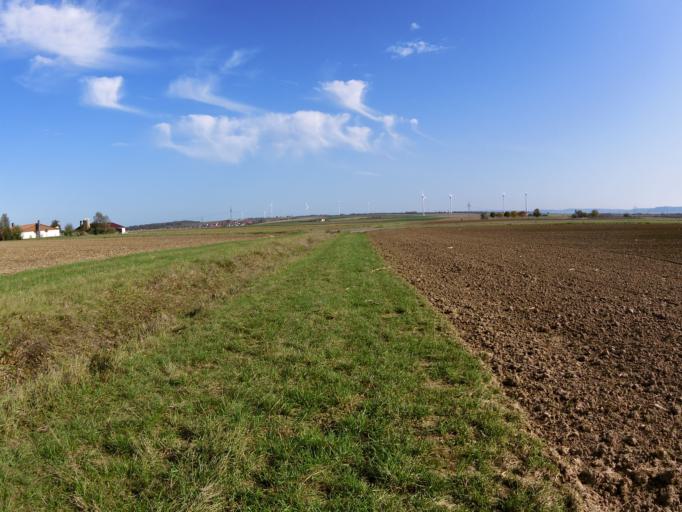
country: DE
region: Bavaria
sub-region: Regierungsbezirk Unterfranken
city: Biebelried
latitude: 49.7484
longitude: 10.0622
